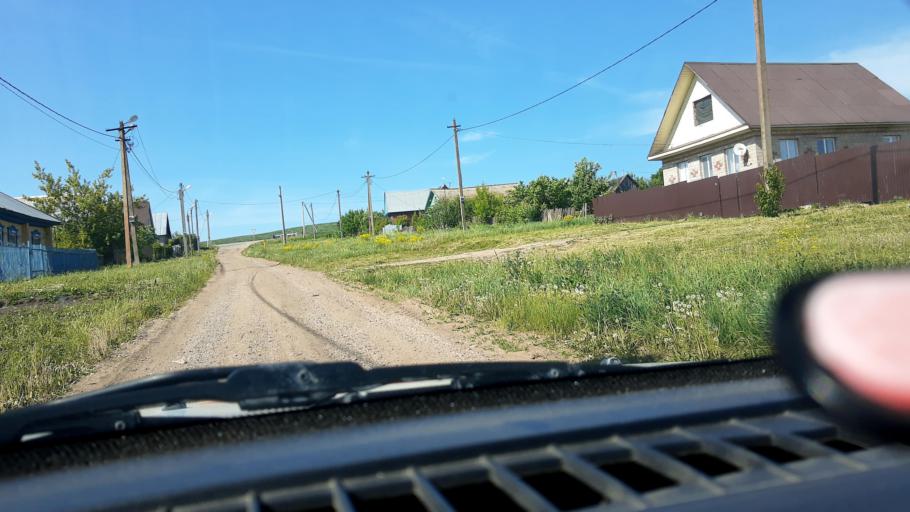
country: RU
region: Bashkortostan
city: Iglino
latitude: 54.8830
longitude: 56.3063
